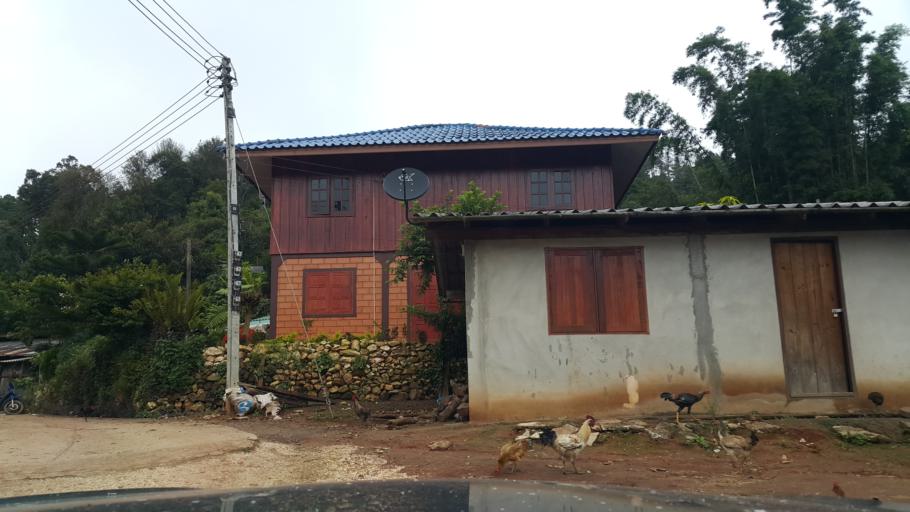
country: TH
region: Chiang Mai
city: Samoeng
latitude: 18.8797
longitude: 98.5133
